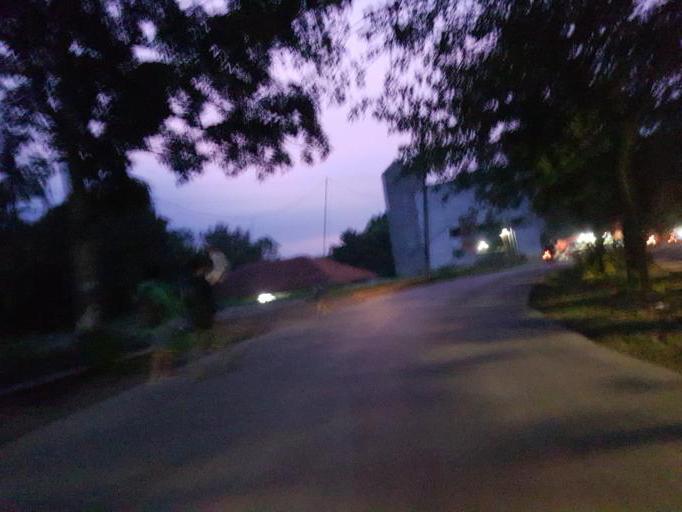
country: ID
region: West Java
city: Serpong
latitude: -6.3125
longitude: 106.6595
